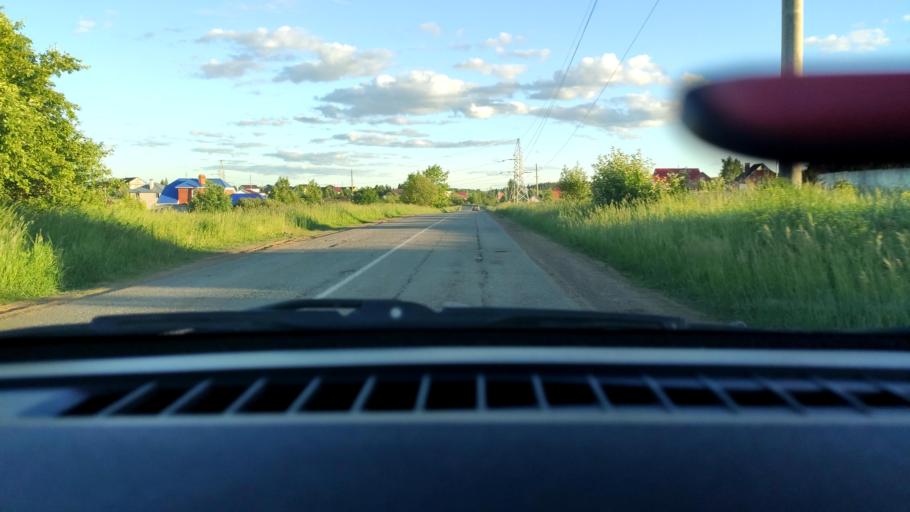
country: RU
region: Perm
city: Kultayevo
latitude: 57.9329
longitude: 55.8636
